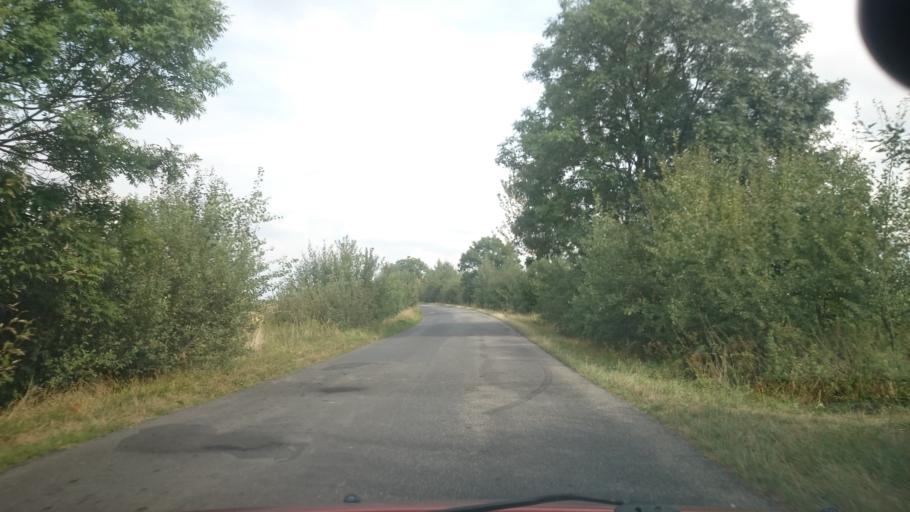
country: PL
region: Opole Voivodeship
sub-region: Powiat nyski
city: Otmuchow
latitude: 50.5000
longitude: 17.2070
